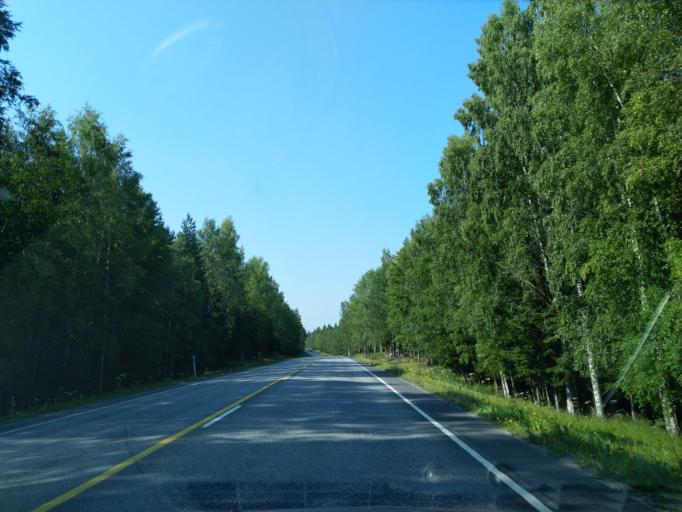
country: FI
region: Satakunta
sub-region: Pori
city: Noormarkku
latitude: 61.6170
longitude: 21.8992
